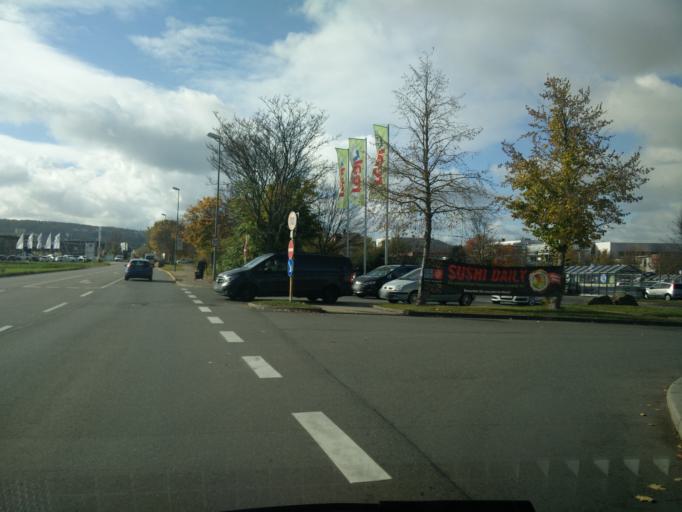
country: DE
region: Baden-Wuerttemberg
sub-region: Regierungsbezirk Stuttgart
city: Gerlingen
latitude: 48.8063
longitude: 9.0776
